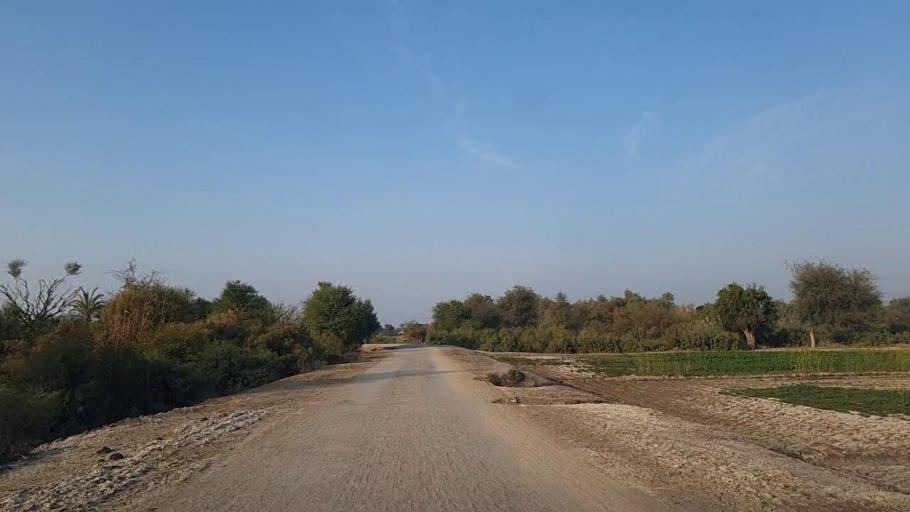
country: PK
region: Sindh
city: Jam Sahib
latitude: 26.3935
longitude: 68.5432
